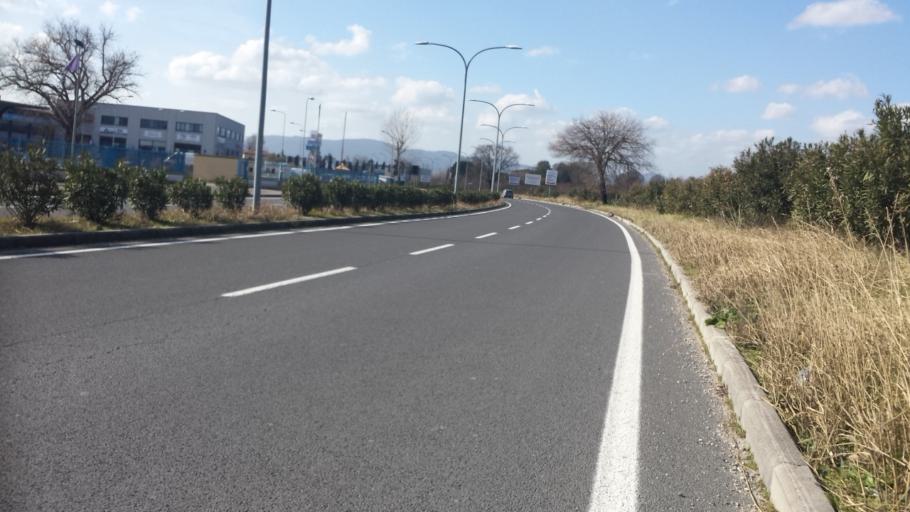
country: IT
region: Umbria
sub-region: Provincia di Terni
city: Terni
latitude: 42.5676
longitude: 12.6025
